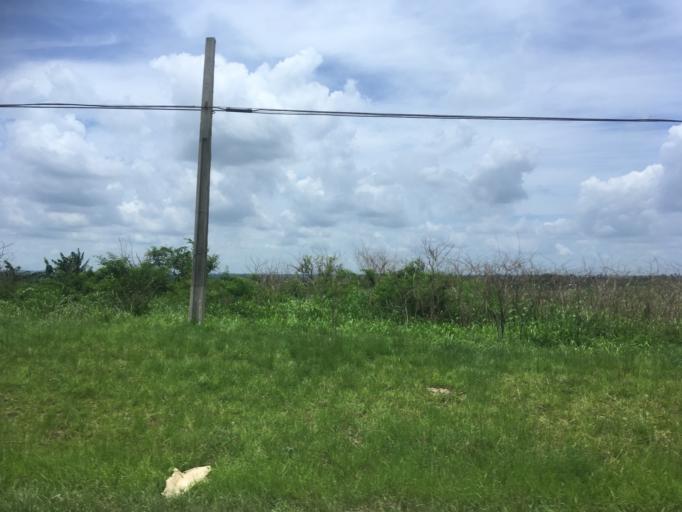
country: CU
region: Villa Clara
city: Esperanza
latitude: 22.4163
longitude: -80.0431
